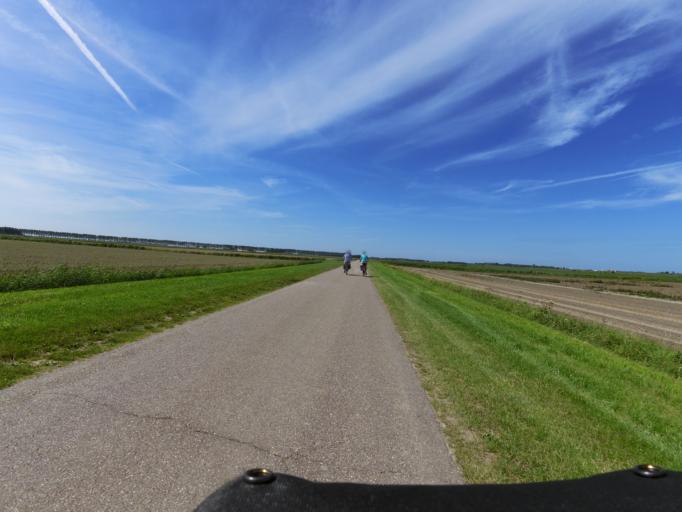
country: NL
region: South Holland
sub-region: Gemeente Goeree-Overflakkee
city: Dirksland
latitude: 51.7998
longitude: 4.0782
